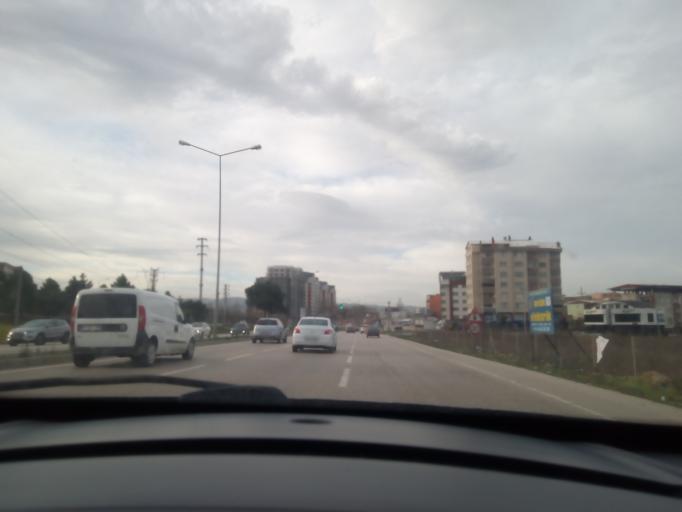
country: TR
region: Bursa
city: Niluefer
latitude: 40.2295
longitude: 28.9641
